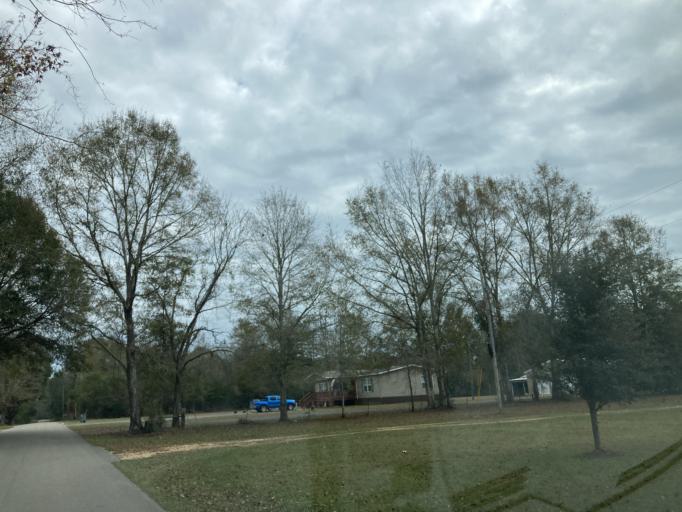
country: US
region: Mississippi
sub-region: Perry County
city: New Augusta
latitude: 31.0654
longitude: -89.1979
